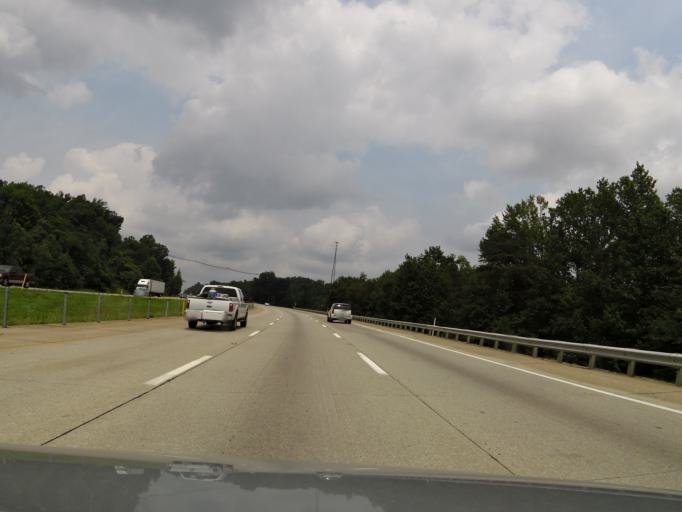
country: US
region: Kentucky
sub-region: Bullitt County
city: Shepherdsville
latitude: 37.9522
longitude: -85.6893
